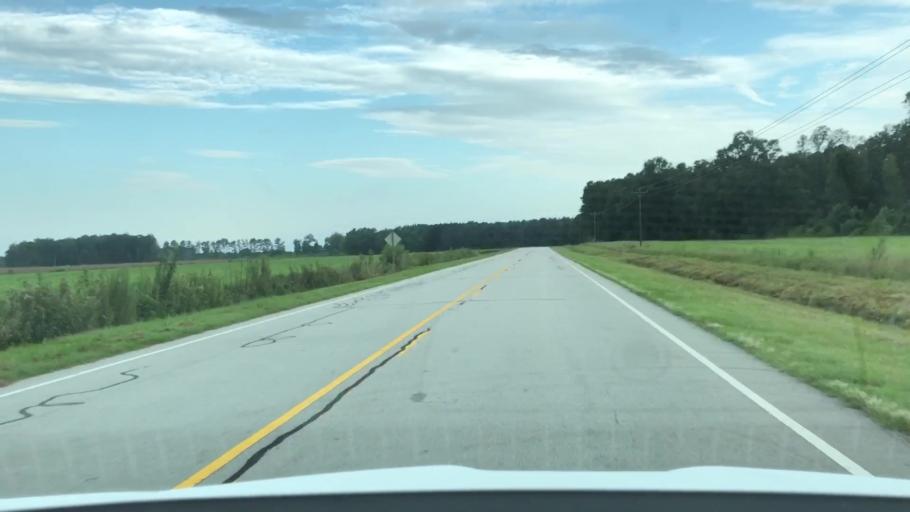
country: US
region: North Carolina
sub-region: Jones County
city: Trenton
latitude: 35.1076
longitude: -77.5021
